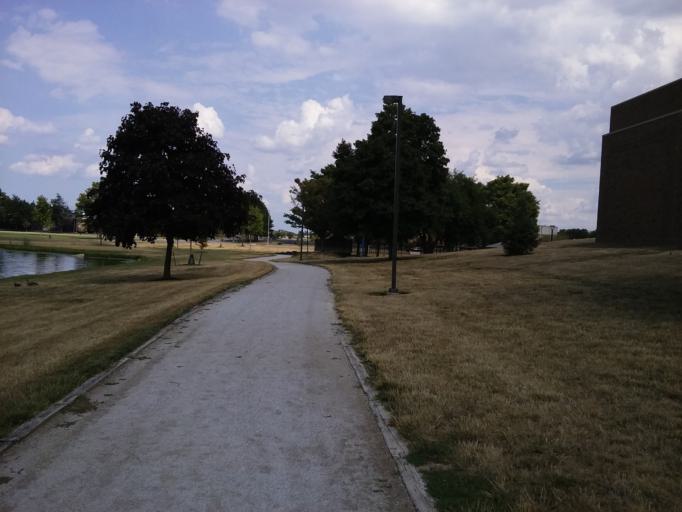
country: US
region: Ohio
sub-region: Wood County
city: Bowling Green
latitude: 41.3799
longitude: -83.6319
